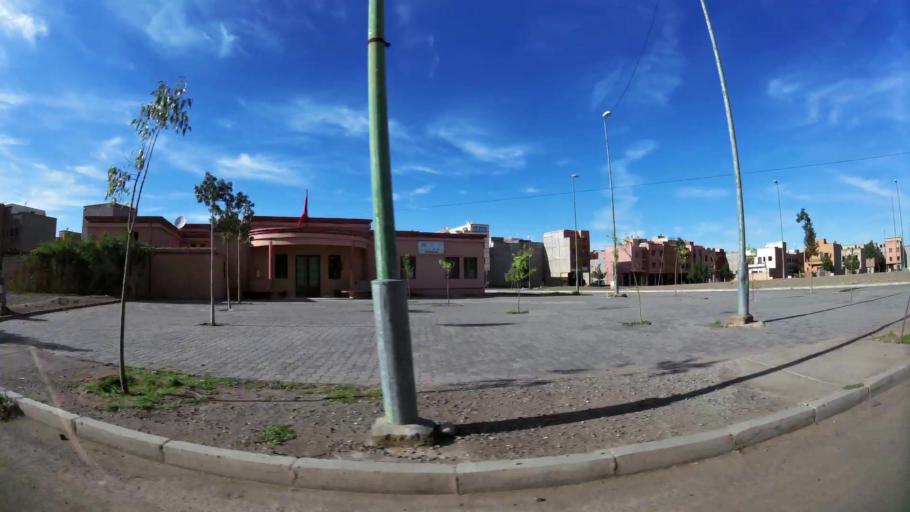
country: MA
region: Marrakech-Tensift-Al Haouz
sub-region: Marrakech
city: Marrakesh
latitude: 31.6878
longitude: -8.0657
